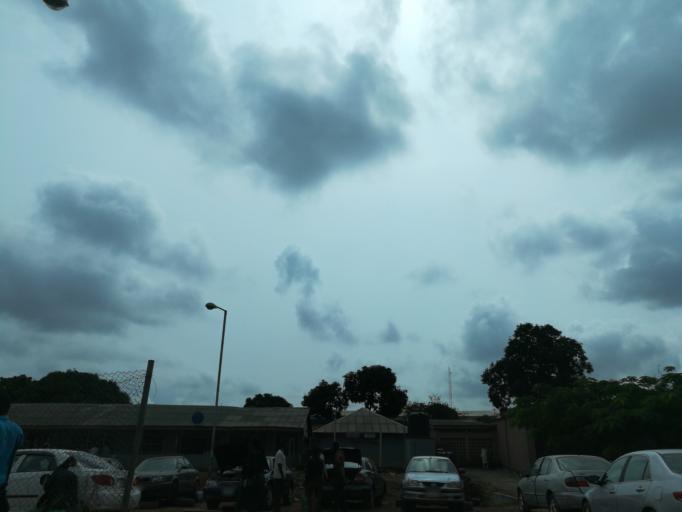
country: NG
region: Lagos
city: Oshodi
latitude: 6.5742
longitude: 3.3234
